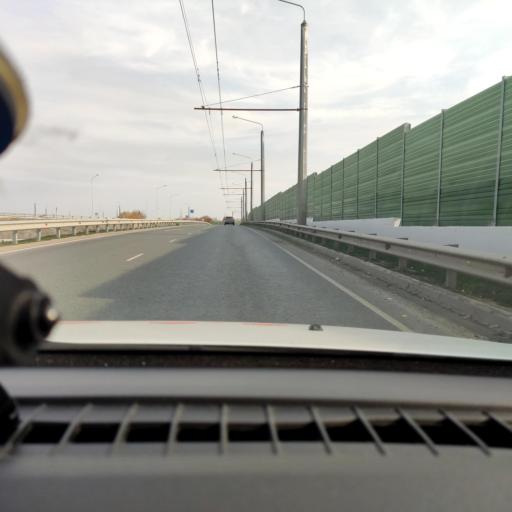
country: RU
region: Samara
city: Rozhdestveno
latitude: 53.1644
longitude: 50.0820
